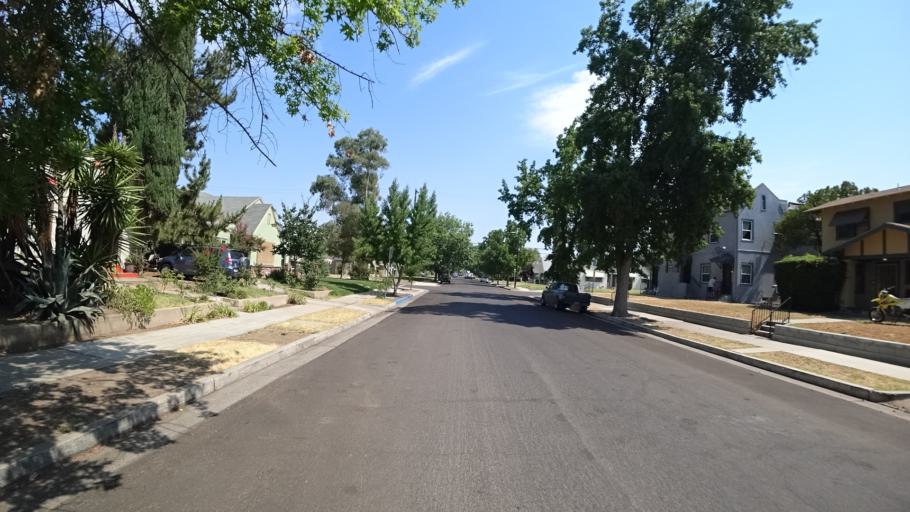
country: US
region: California
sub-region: Fresno County
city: Fresno
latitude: 36.7628
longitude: -119.7968
